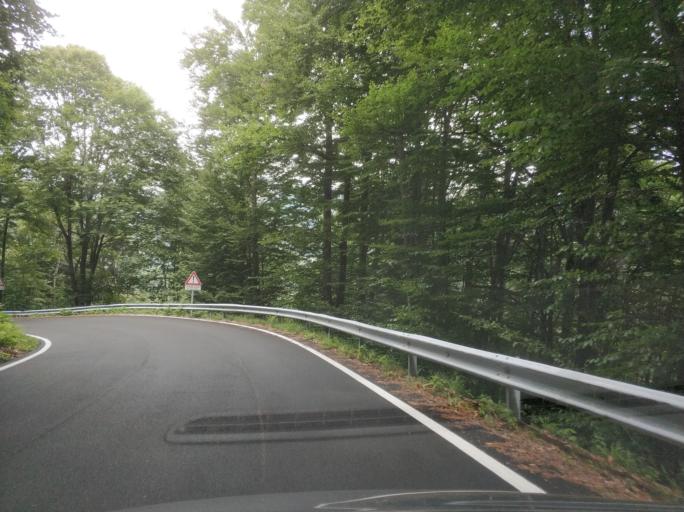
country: IT
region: Piedmont
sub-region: Provincia di Torino
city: Viu
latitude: 45.2240
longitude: 7.3827
